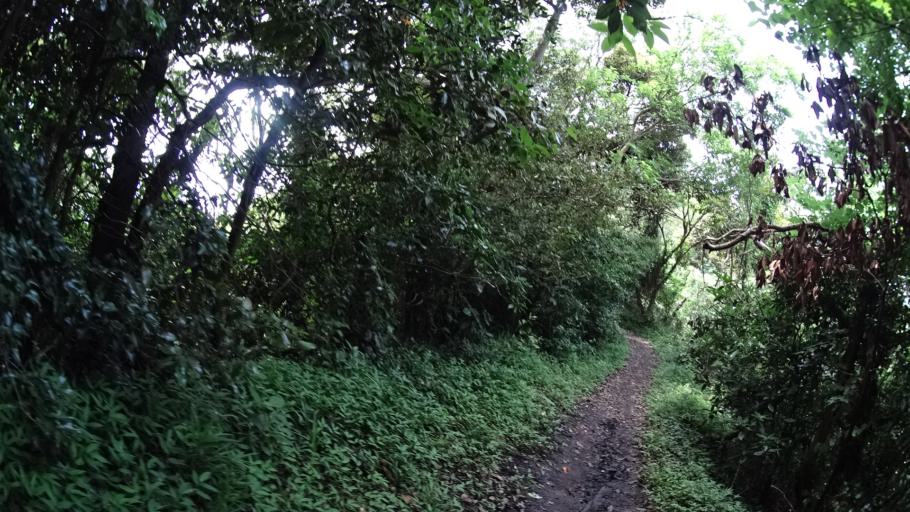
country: JP
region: Kanagawa
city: Yokosuka
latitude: 35.2167
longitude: 139.6679
